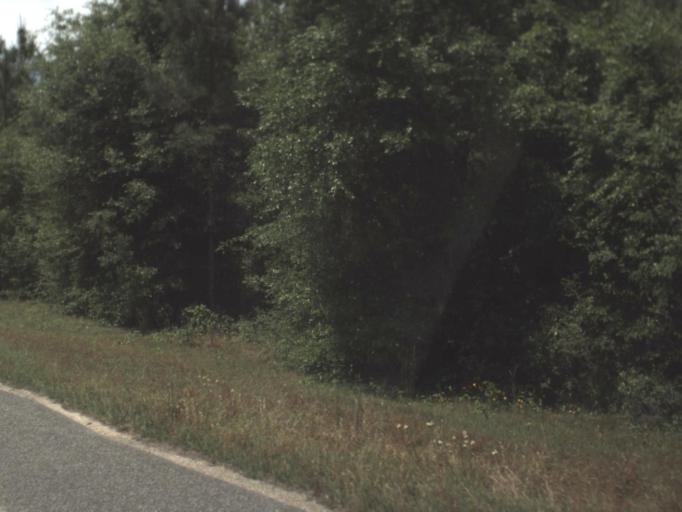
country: US
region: Florida
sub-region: Calhoun County
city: Blountstown
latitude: 30.5707
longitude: -85.1831
